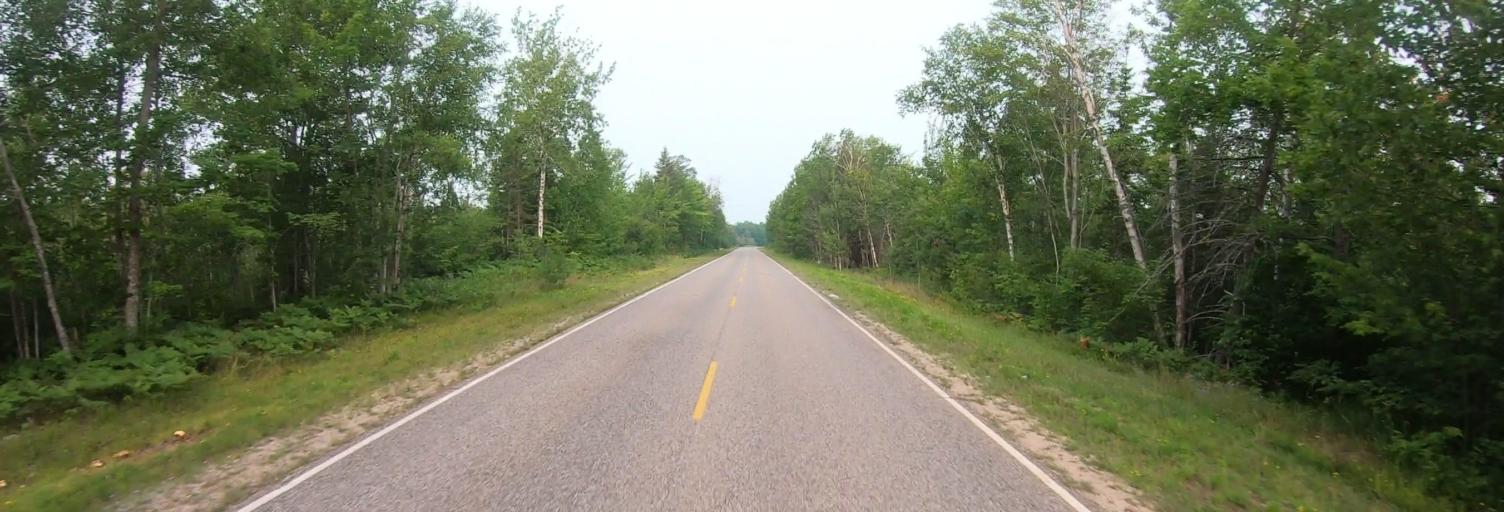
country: US
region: Michigan
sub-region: Chippewa County
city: Sault Ste. Marie
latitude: 46.4646
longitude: -84.8921
